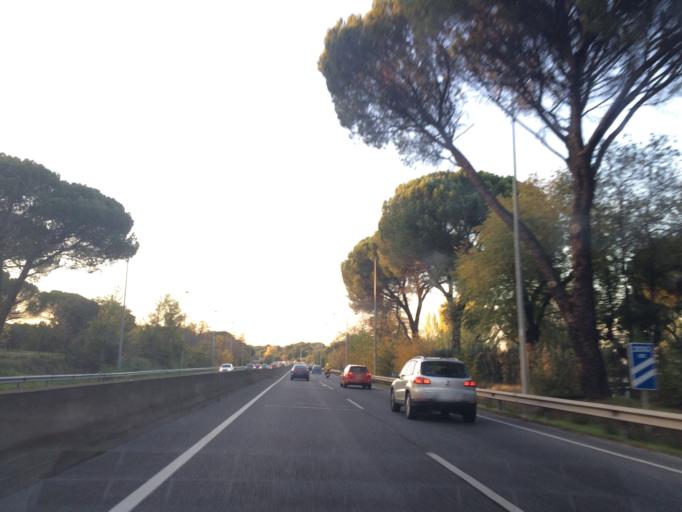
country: ES
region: Madrid
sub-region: Provincia de Madrid
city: Moncloa-Aravaca
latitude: 40.4402
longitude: -3.7449
